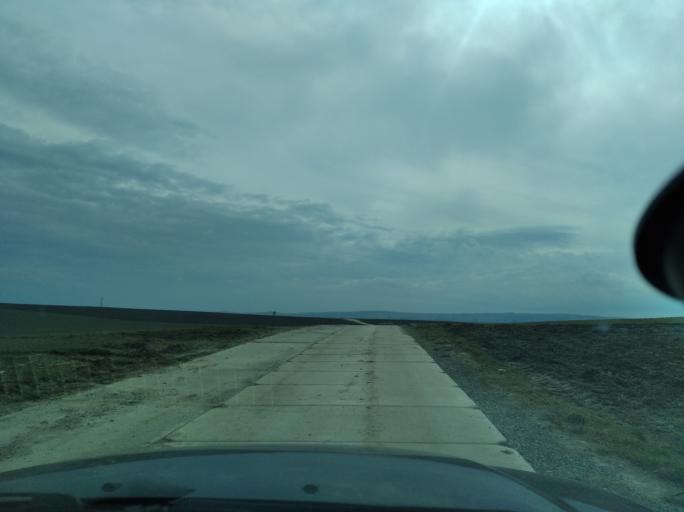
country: PL
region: Subcarpathian Voivodeship
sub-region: Powiat jaroslawski
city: Rokietnica
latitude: 49.9324
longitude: 22.5917
